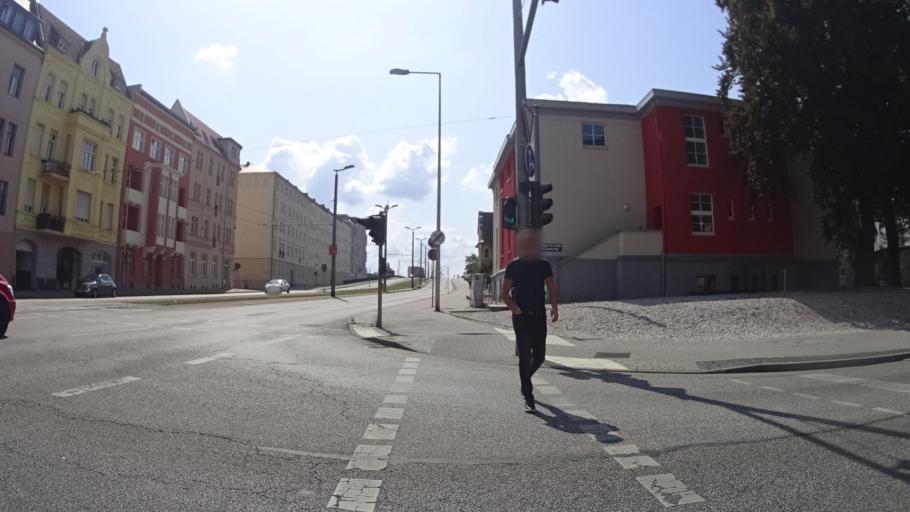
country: DE
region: Brandenburg
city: Cottbus
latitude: 51.7542
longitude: 14.3282
